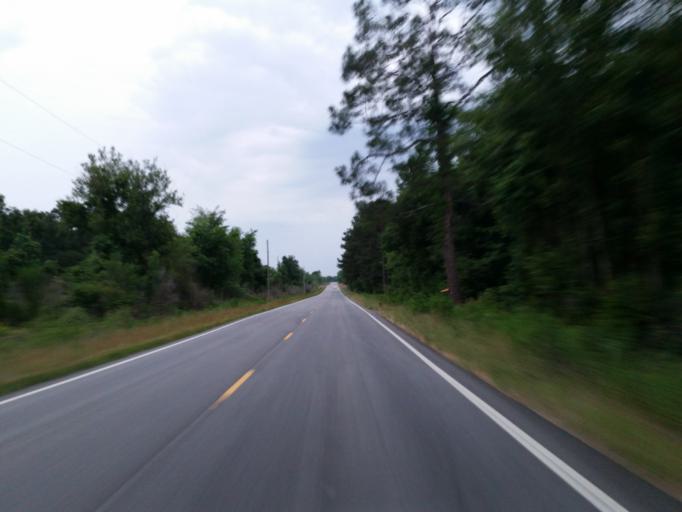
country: US
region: Georgia
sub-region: Turner County
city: Ashburn
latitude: 31.8123
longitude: -83.7213
